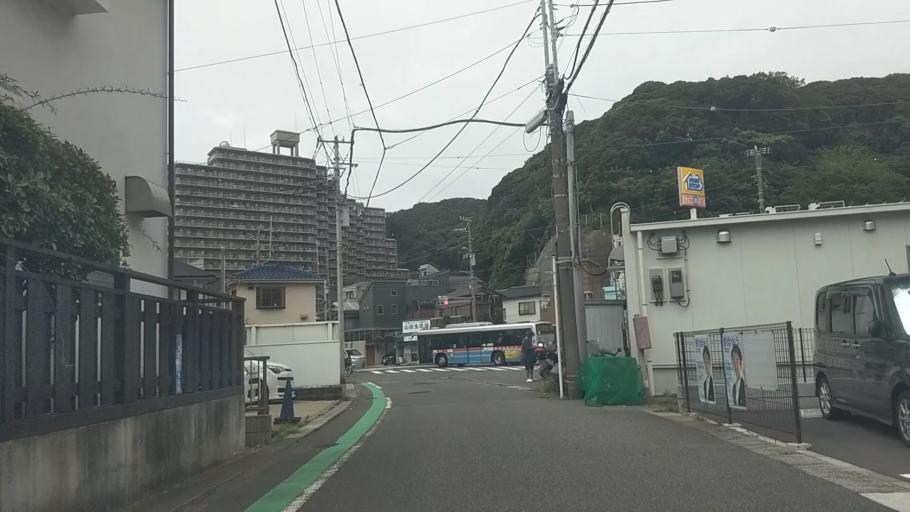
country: JP
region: Kanagawa
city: Yokosuka
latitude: 35.2444
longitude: 139.7215
